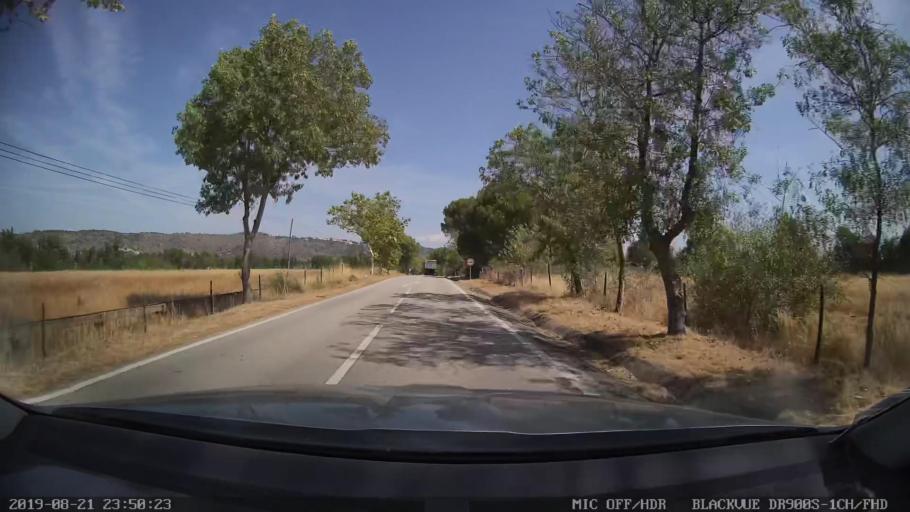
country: PT
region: Castelo Branco
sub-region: Idanha-A-Nova
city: Idanha-a-Nova
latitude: 39.8893
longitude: -7.2428
